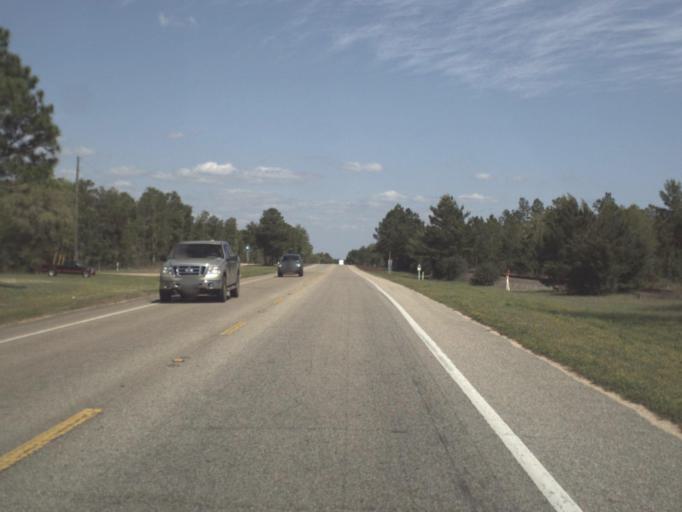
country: US
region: Florida
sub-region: Okaloosa County
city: Crestview
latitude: 30.7439
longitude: -86.4098
